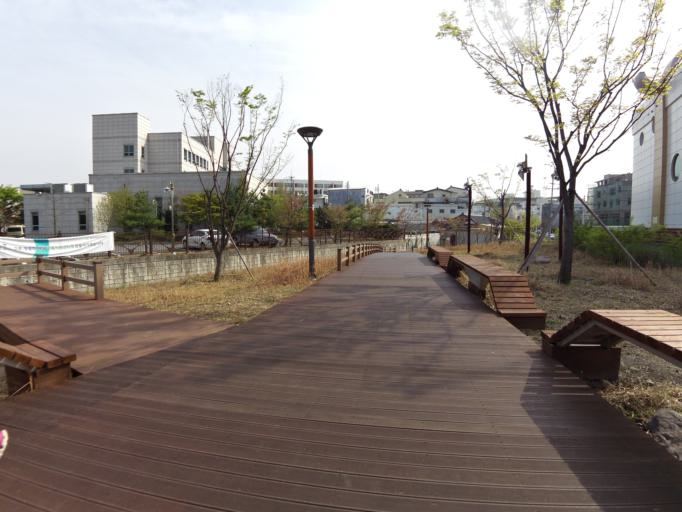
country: KR
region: Daegu
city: Daegu
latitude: 35.8889
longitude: 128.6373
